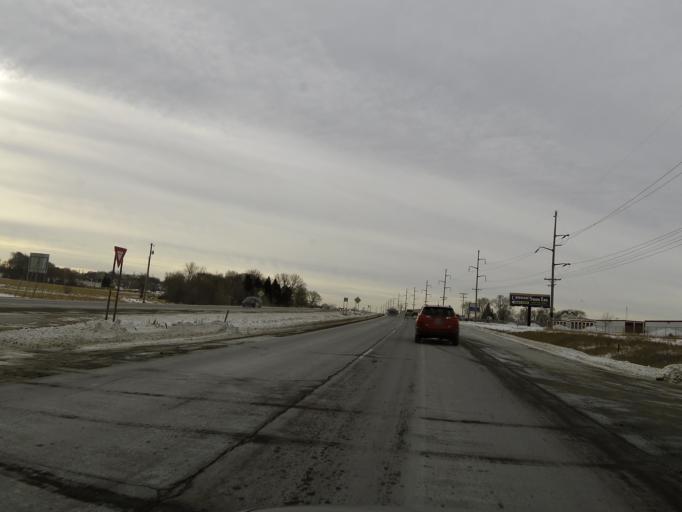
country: US
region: Minnesota
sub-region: Carver County
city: Chaska
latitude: 44.7638
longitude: -93.5806
